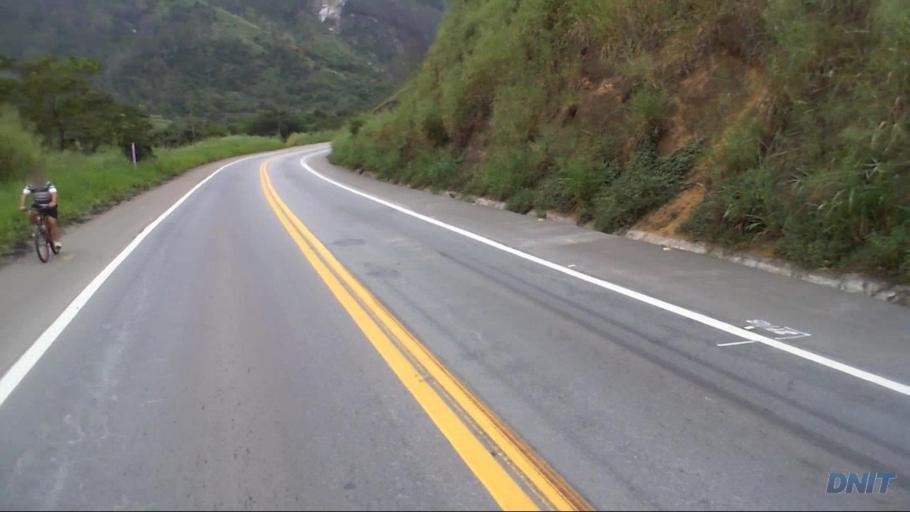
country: BR
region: Minas Gerais
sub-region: Timoteo
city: Timoteo
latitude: -19.5562
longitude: -42.7106
